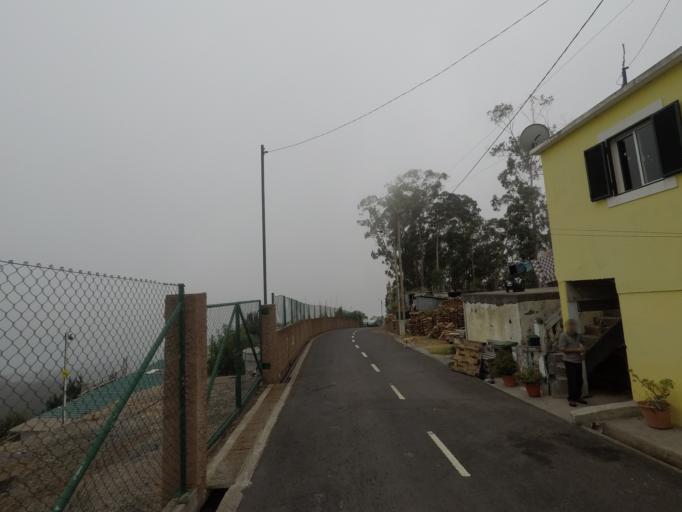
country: PT
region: Madeira
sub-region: Camara de Lobos
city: Curral das Freiras
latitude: 32.6891
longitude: -16.9475
